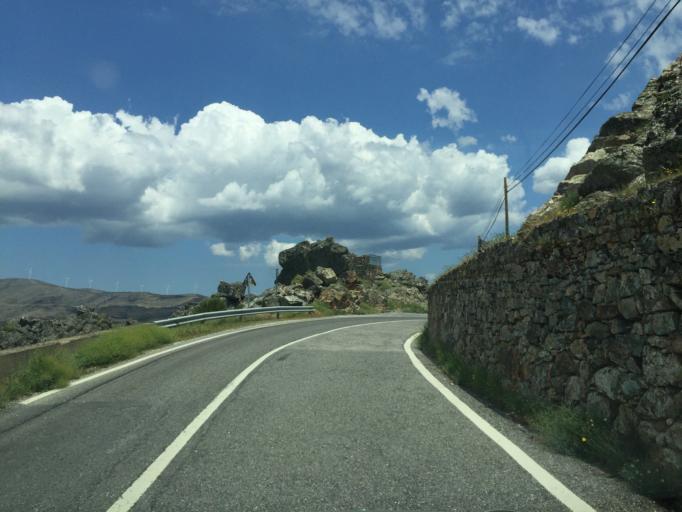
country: PT
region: Coimbra
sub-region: Pampilhosa da Serra
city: Pampilhosa da Serra
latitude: 40.0874
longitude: -7.8574
